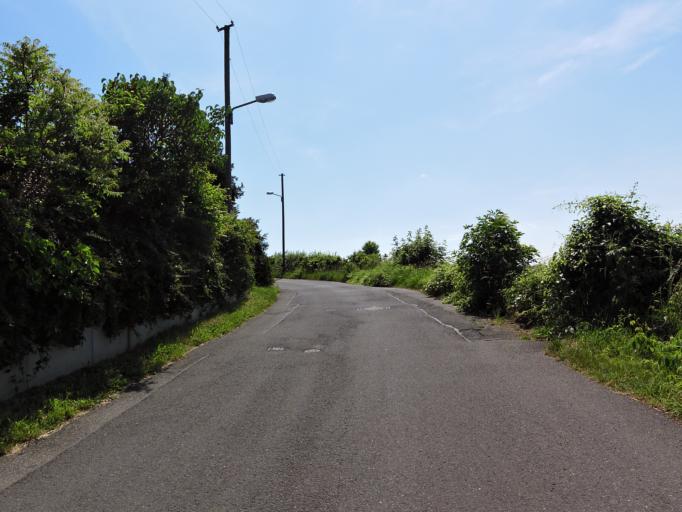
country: DE
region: Bavaria
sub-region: Regierungsbezirk Unterfranken
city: Wuerzburg
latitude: 49.7735
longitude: 9.9473
